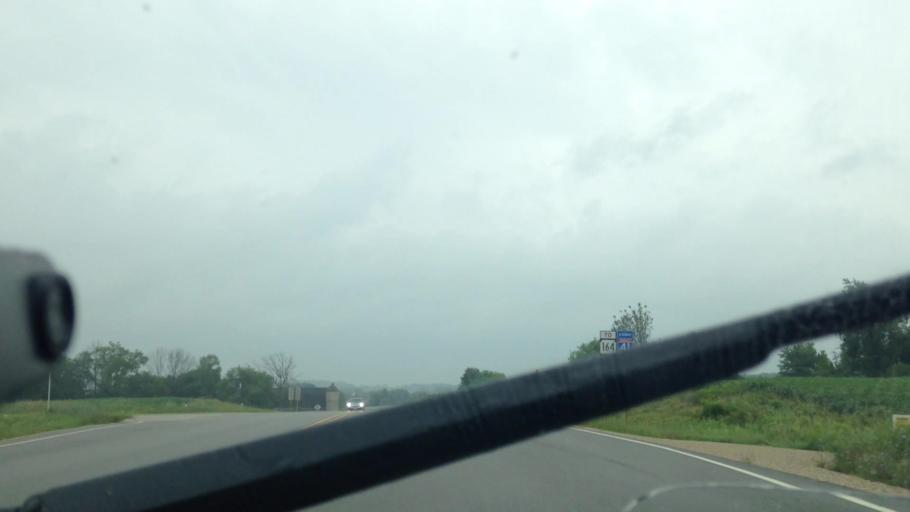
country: US
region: Wisconsin
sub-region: Washington County
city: Slinger
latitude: 43.3146
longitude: -88.2639
